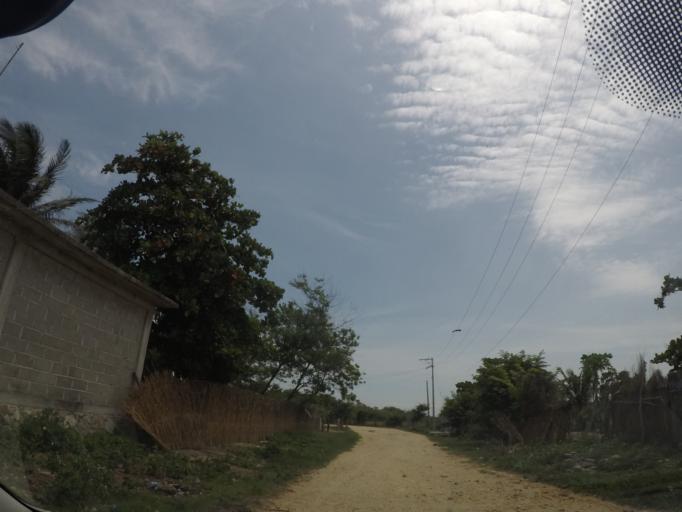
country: MX
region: Oaxaca
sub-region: San Mateo del Mar
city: Colonia Juarez
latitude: 16.2099
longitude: -95.0354
